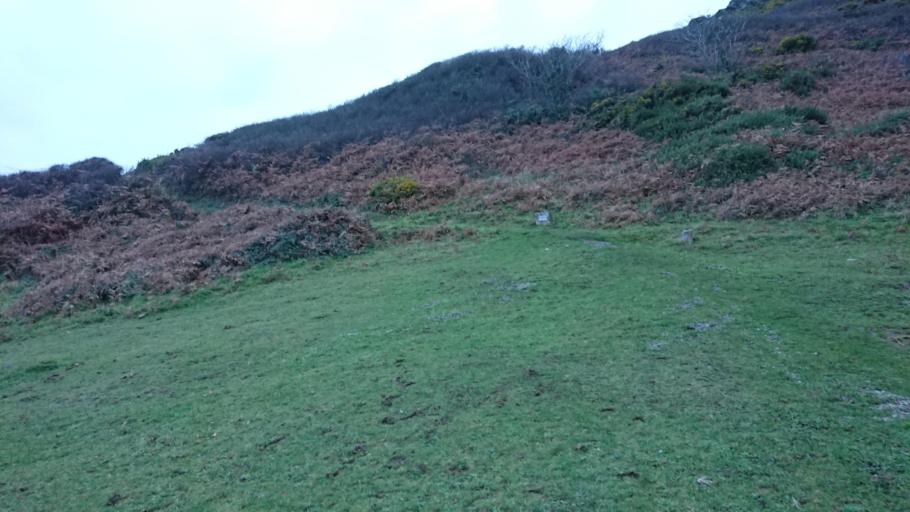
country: GB
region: England
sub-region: Cornwall
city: Fowey
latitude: 50.3288
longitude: -4.5633
